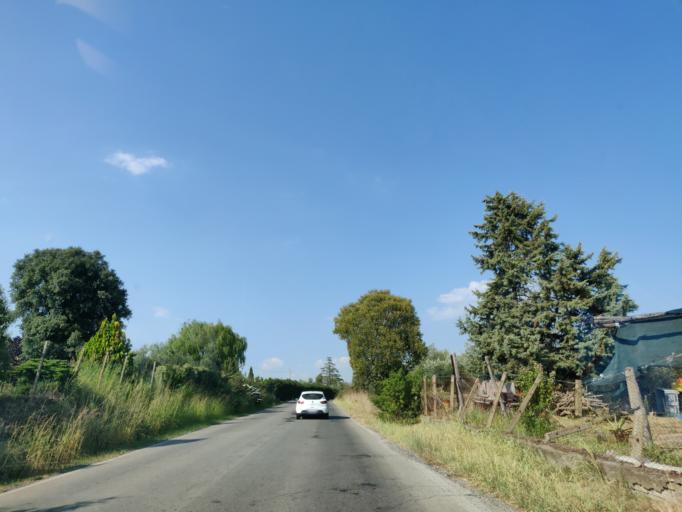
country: IT
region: Latium
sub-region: Provincia di Viterbo
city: Canino
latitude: 42.4164
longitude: 11.7036
